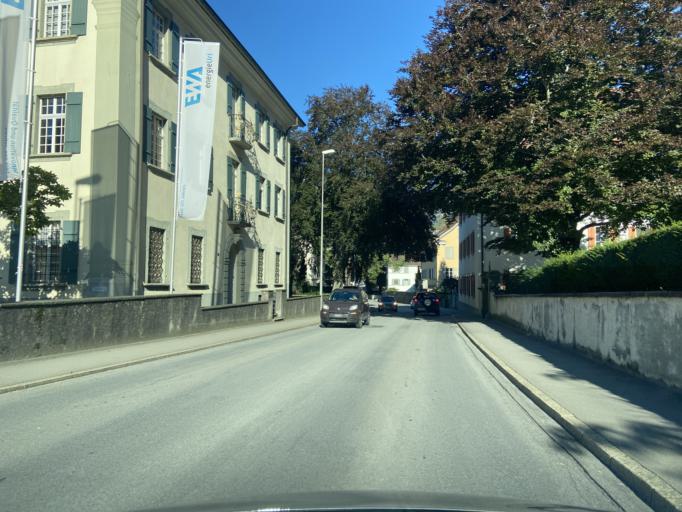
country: CH
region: Uri
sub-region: Uri
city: Altdorf
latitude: 46.8827
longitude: 8.6406
